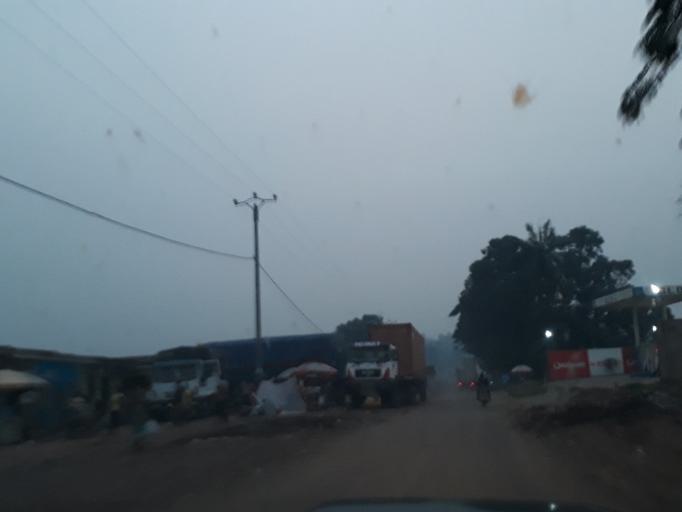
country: CD
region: Bandundu
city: Kikwit
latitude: -5.0398
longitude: 18.8362
